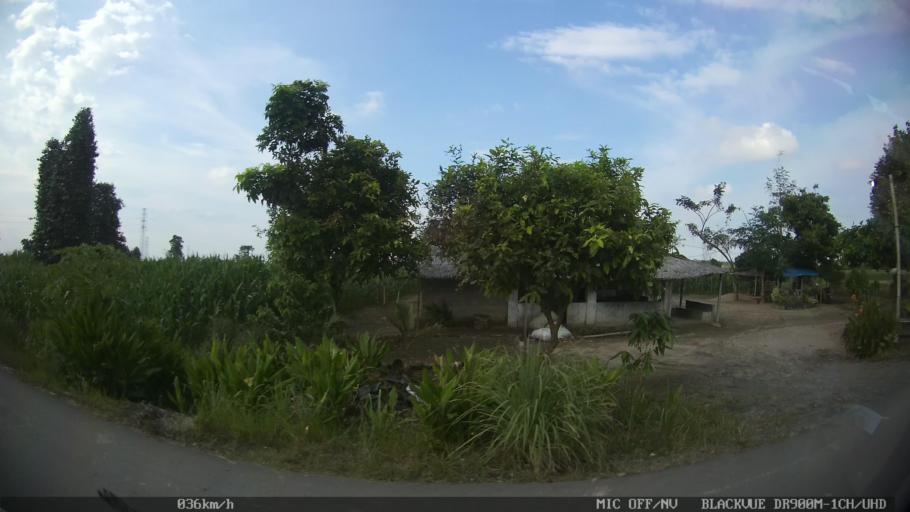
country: ID
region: North Sumatra
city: Percut
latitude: 3.5672
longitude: 98.7850
